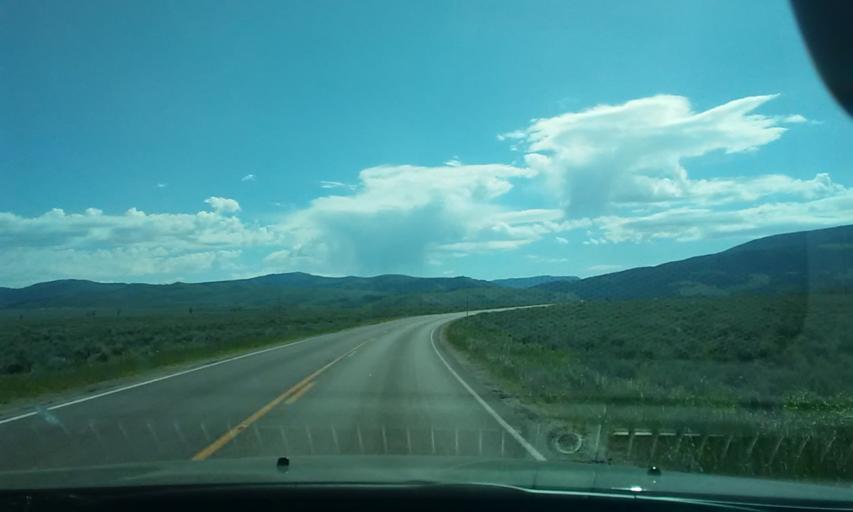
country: US
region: Wyoming
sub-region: Teton County
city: Jackson
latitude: 43.6250
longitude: -110.6630
